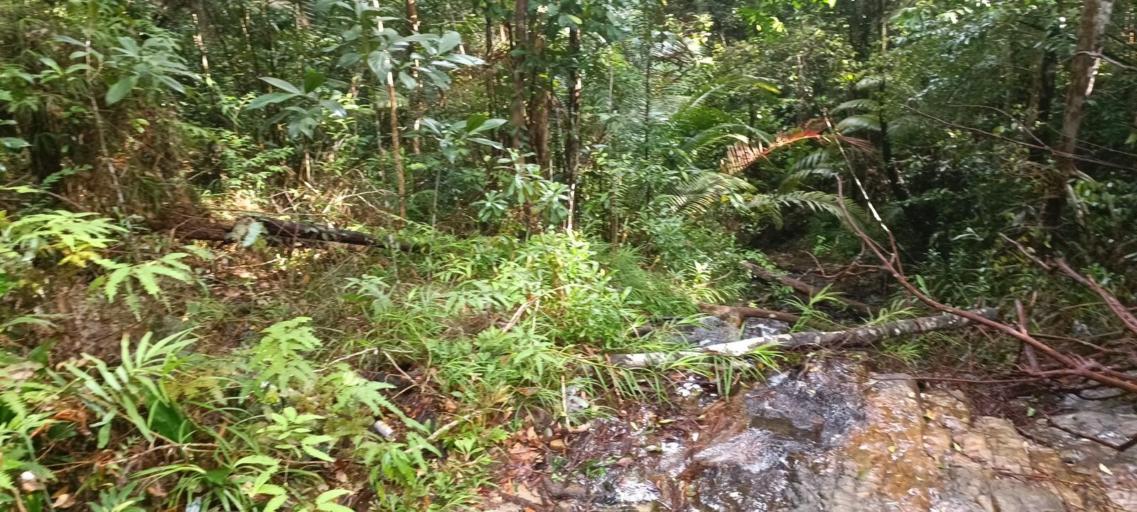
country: MY
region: Penang
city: Tanjung Tokong
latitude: 5.4600
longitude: 100.1977
